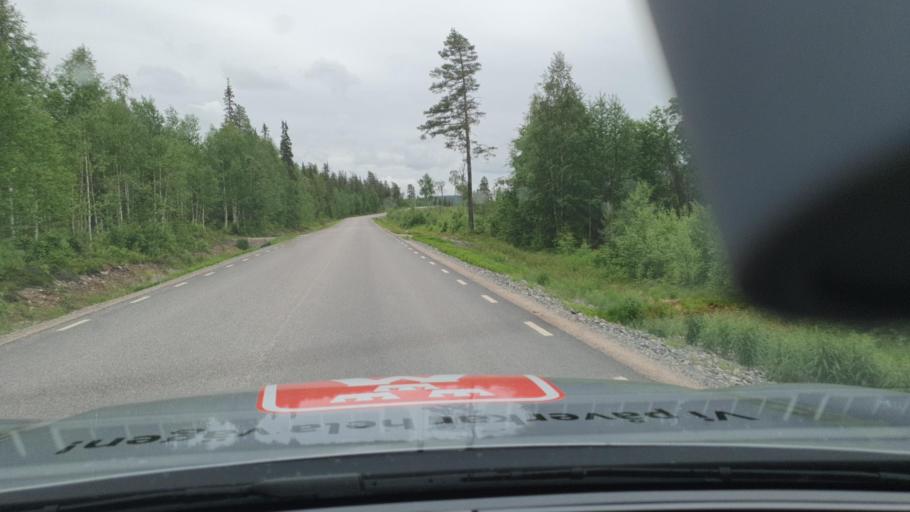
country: SE
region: Norrbotten
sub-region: Overtornea Kommun
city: OEvertornea
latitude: 66.5856
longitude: 23.3238
